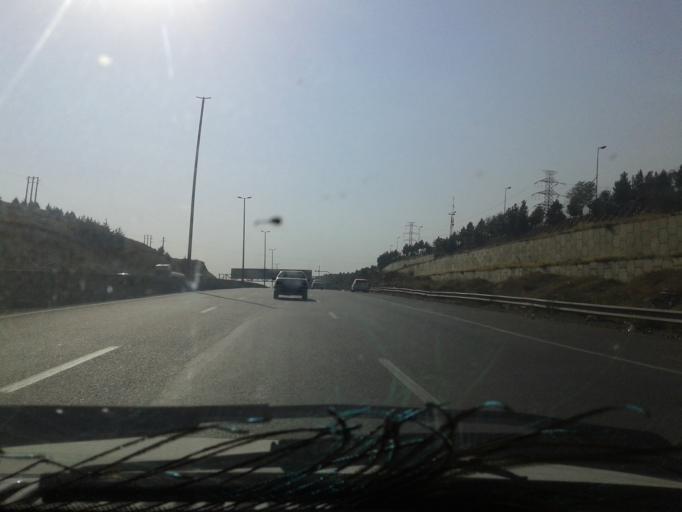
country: IR
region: Tehran
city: Tehran
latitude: 35.7333
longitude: 51.6632
